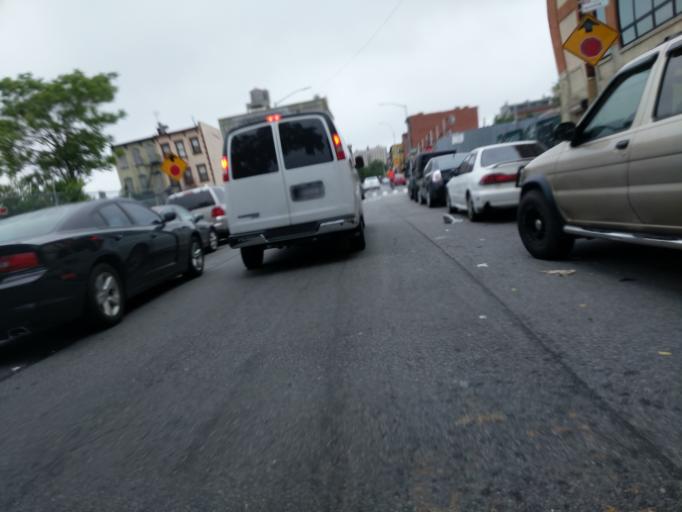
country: US
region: New York
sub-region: Kings County
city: Brooklyn
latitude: 40.6802
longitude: -73.9616
